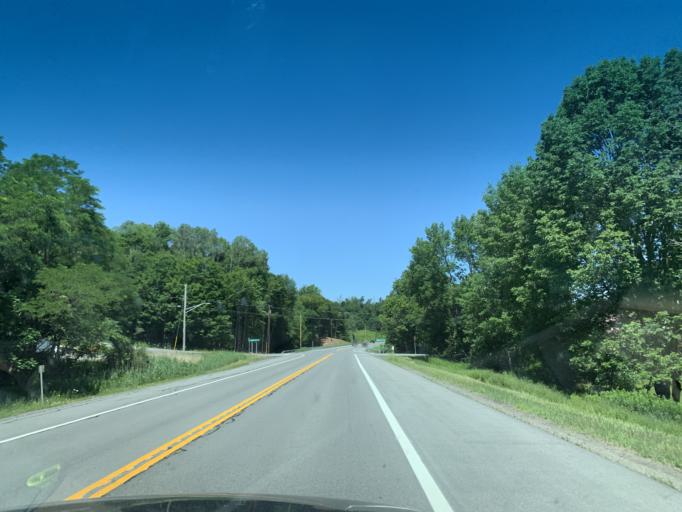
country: US
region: New York
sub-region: Oneida County
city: Chadwicks
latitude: 42.9657
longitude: -75.2497
